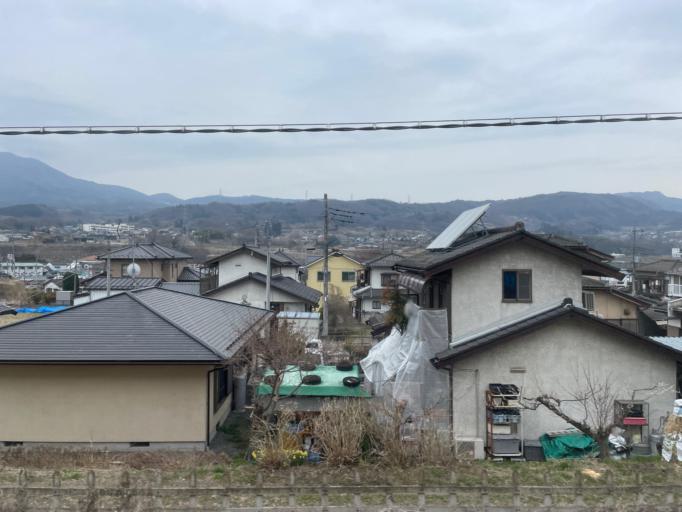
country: JP
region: Gunma
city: Numata
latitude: 36.6357
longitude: 139.0398
